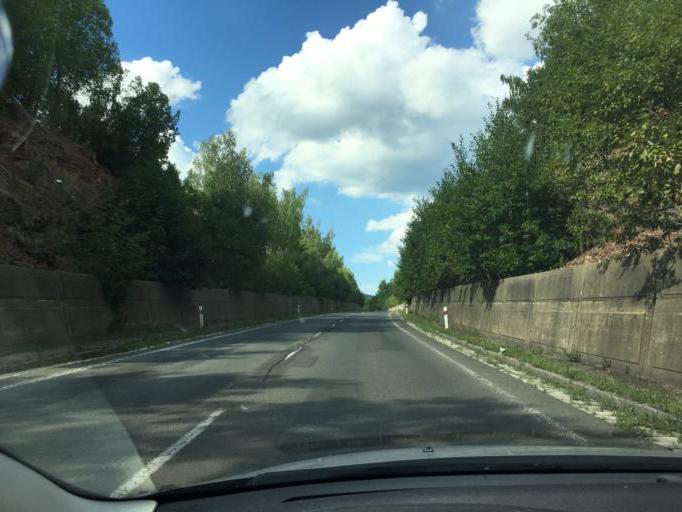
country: CZ
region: Kralovehradecky
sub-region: Okres Trutnov
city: Vrchlabi
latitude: 50.6232
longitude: 15.5965
